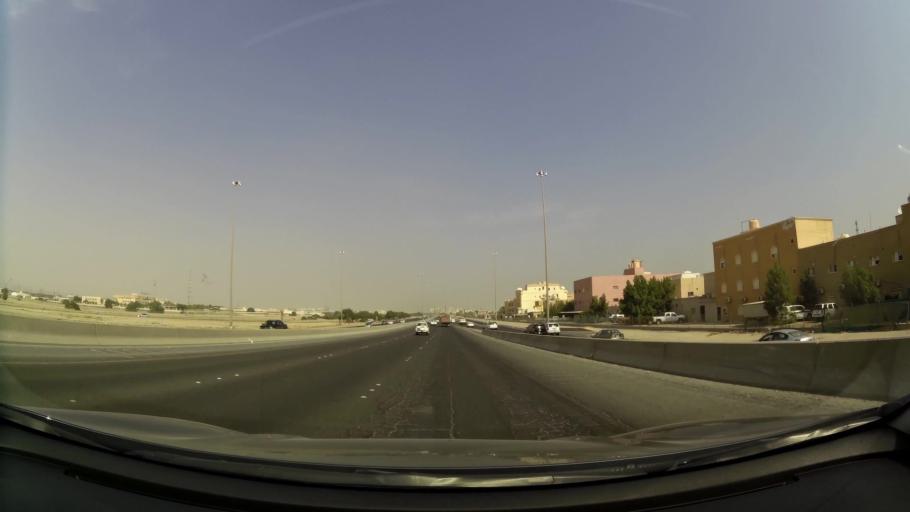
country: KW
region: Al Ahmadi
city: Al Fahahil
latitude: 29.0758
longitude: 48.1126
